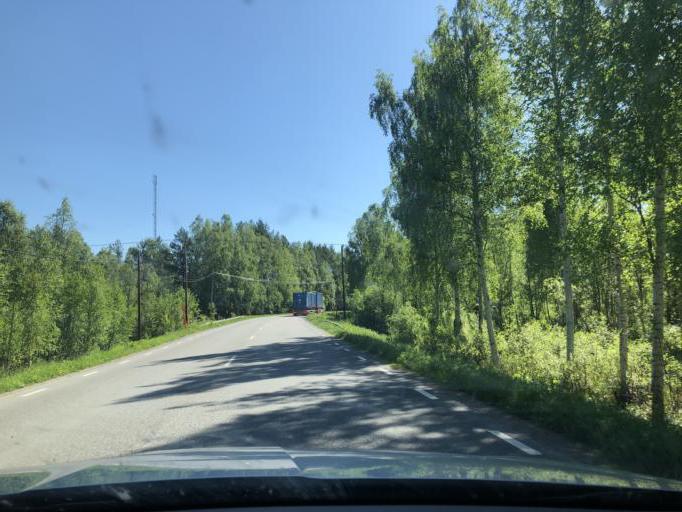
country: SE
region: Norrbotten
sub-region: Lulea Kommun
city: Sodra Sunderbyn
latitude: 65.6644
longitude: 21.9656
